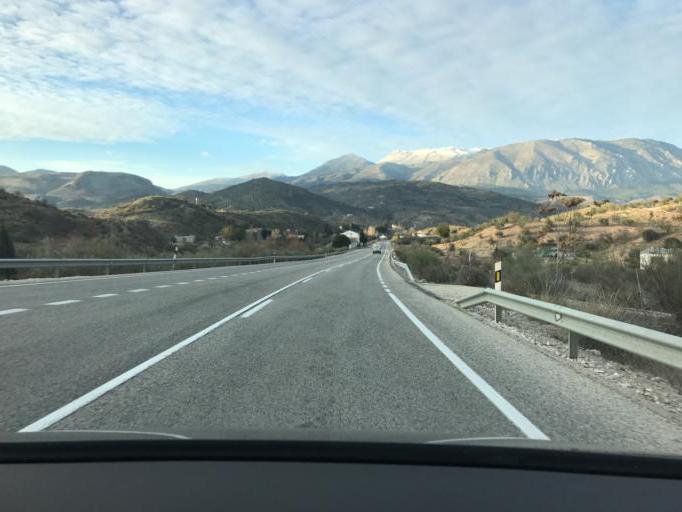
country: ES
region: Andalusia
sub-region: Provincia de Jaen
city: Huelma
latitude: 37.6410
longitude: -3.4152
